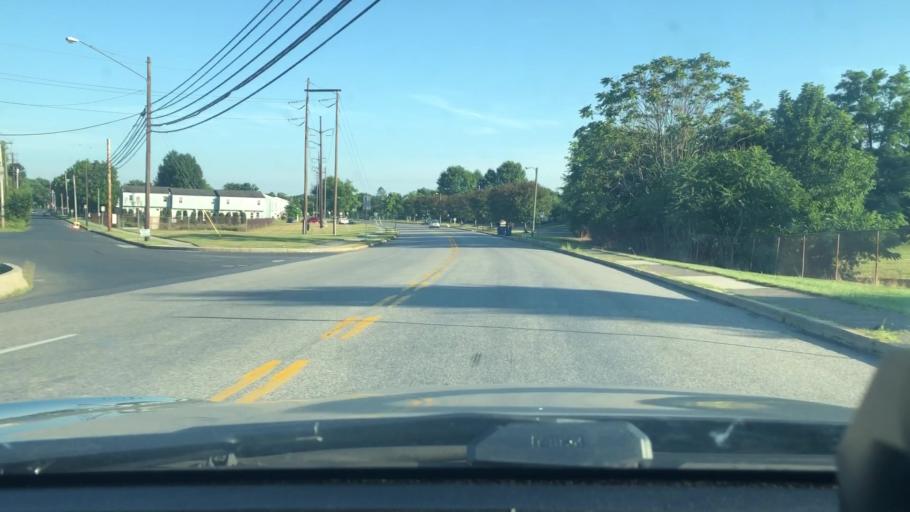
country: US
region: Pennsylvania
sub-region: Cumberland County
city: Mechanicsburg
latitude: 40.2237
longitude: -77.0077
